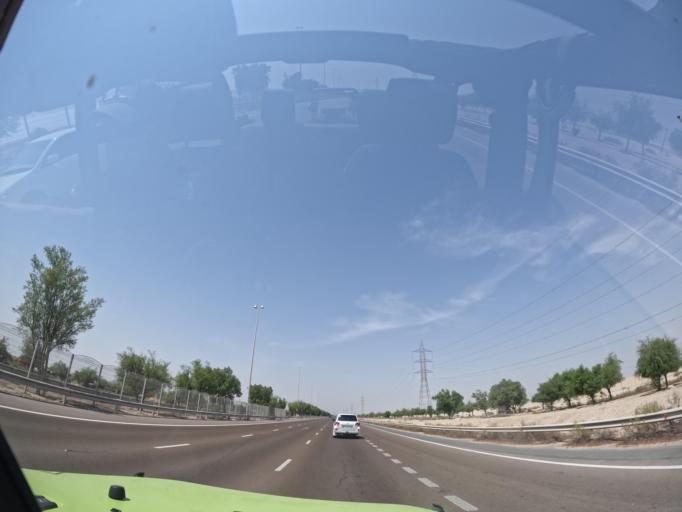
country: AE
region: Abu Dhabi
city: Abu Dhabi
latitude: 24.2191
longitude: 54.8494
